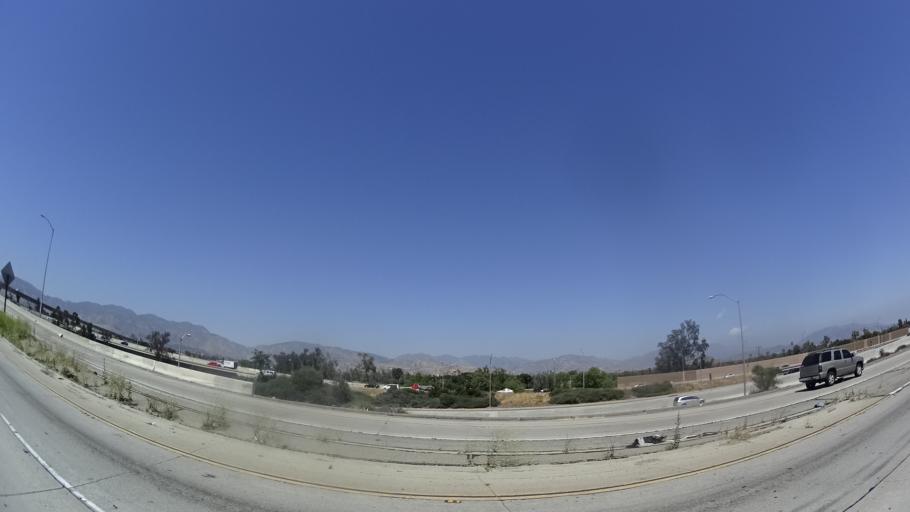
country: US
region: California
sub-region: Los Angeles County
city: San Fernando
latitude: 34.2637
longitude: -118.4421
